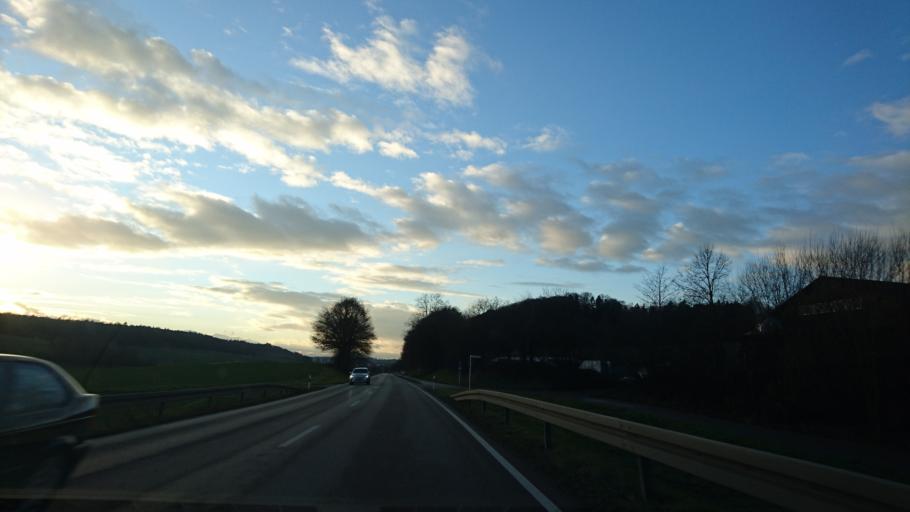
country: DE
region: Bavaria
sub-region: Swabia
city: Zusmarshausen
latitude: 48.3966
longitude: 10.6306
